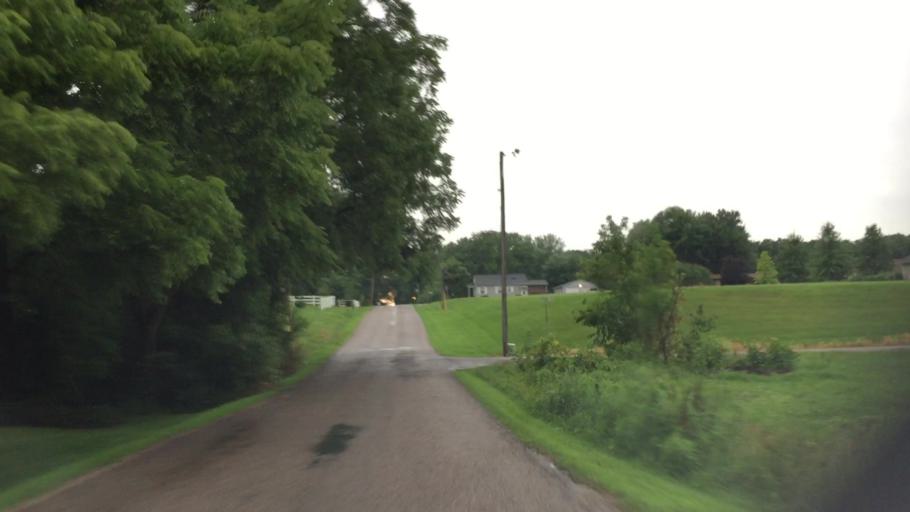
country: US
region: Illinois
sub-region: Hancock County
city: Nauvoo
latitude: 40.5428
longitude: -91.3719
